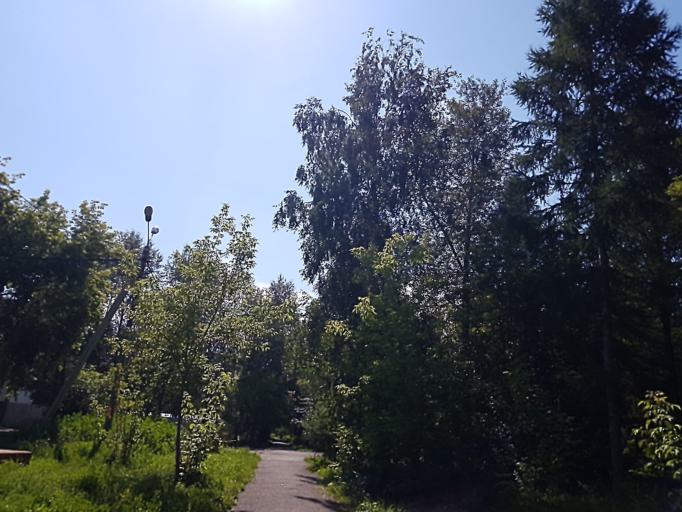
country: RU
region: Irkutsk
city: Usol'ye-Sibirskoye
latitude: 52.7567
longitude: 103.6347
